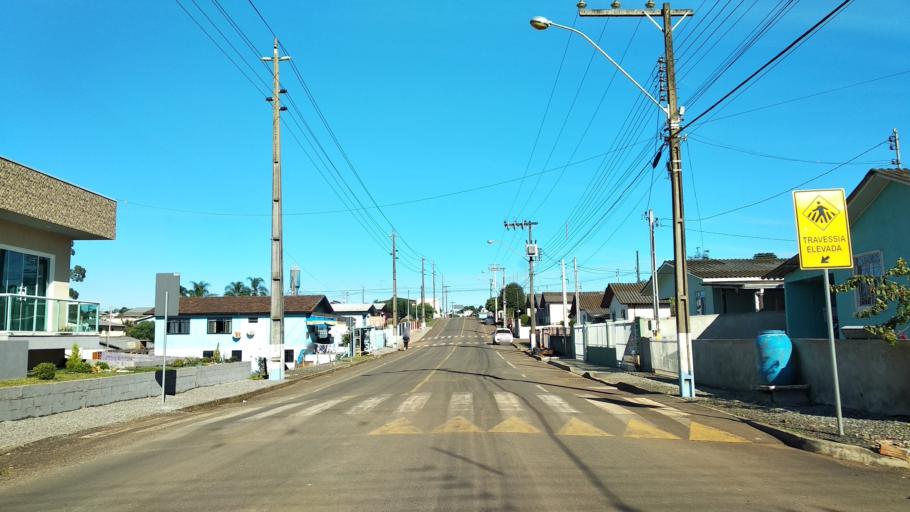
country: BR
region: Santa Catarina
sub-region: Campos Novos
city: Campos Novos
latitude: -27.3862
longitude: -51.2099
